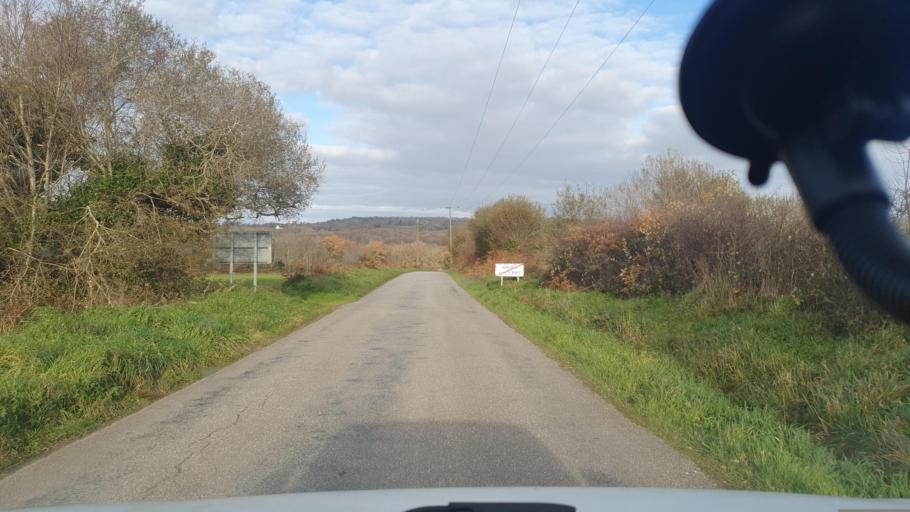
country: FR
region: Brittany
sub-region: Departement du Finistere
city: Briec
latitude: 48.1084
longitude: -3.9968
